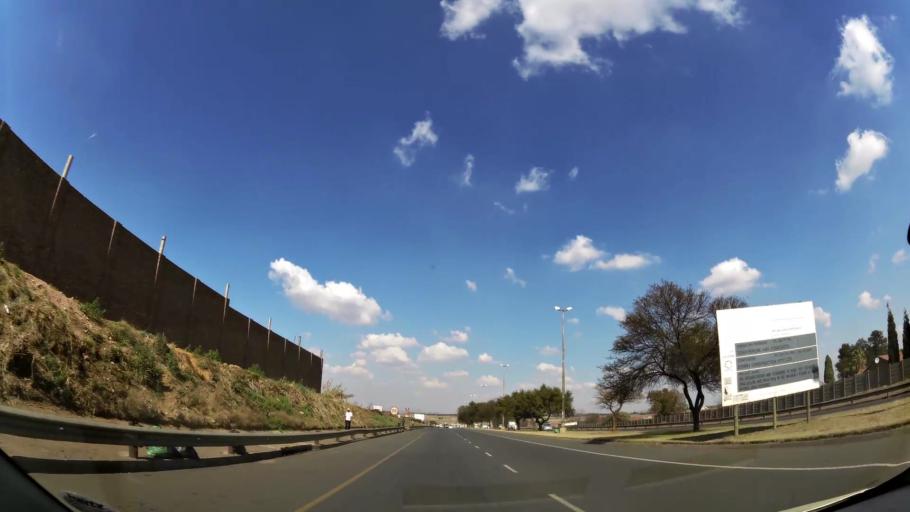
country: ZA
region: Mpumalanga
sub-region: Nkangala District Municipality
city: Witbank
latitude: -25.9231
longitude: 29.2341
